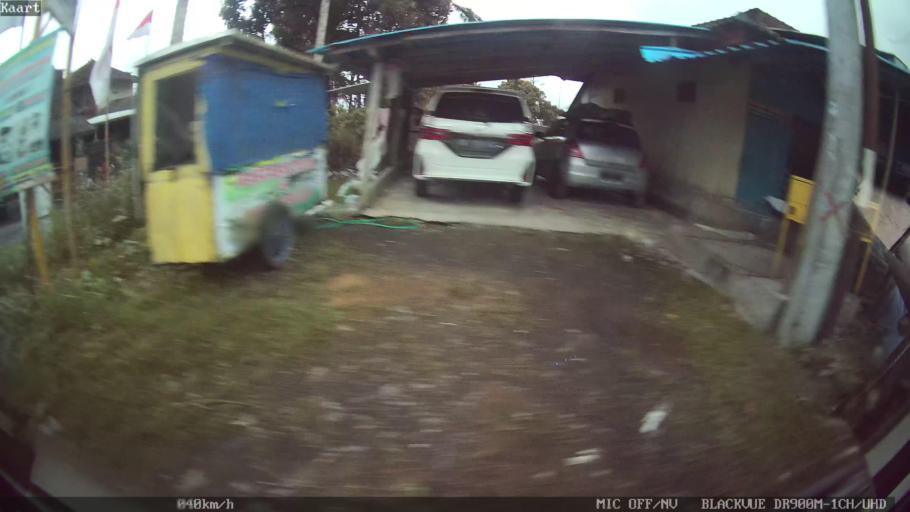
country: ID
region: Bali
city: Peneng
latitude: -8.3703
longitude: 115.1726
